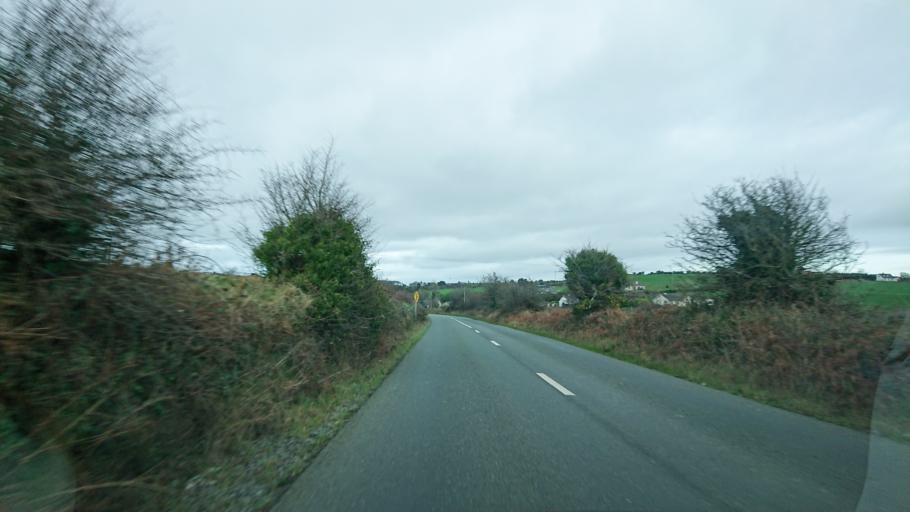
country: IE
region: Leinster
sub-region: Kilkenny
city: Mooncoin
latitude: 52.2161
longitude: -7.2402
